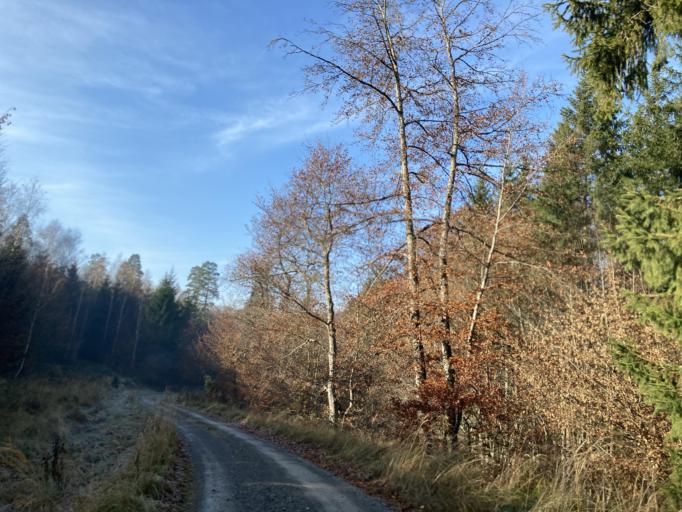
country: DE
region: Baden-Wuerttemberg
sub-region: Regierungsbezirk Stuttgart
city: Altdorf
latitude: 48.5859
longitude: 9.0014
